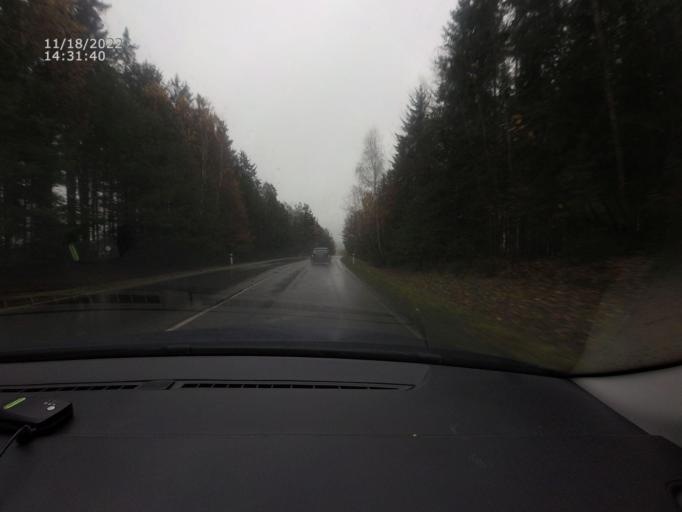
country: CZ
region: Jihocesky
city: Kovarov
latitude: 49.4507
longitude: 14.2657
